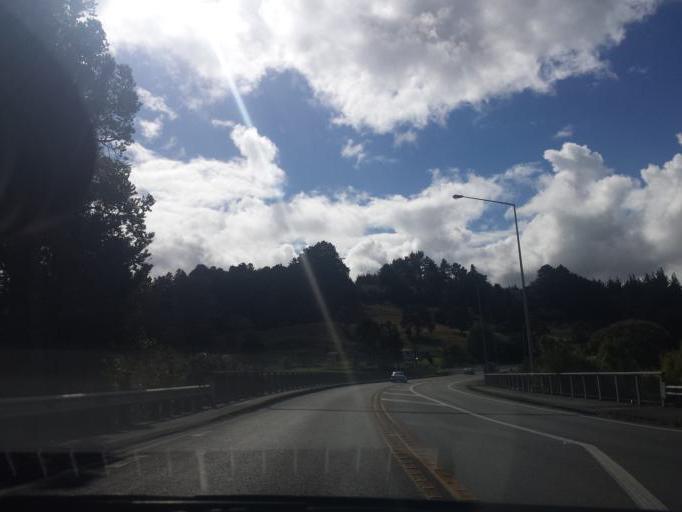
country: NZ
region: Auckland
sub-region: Auckland
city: Warkworth
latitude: -36.5159
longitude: 174.6692
